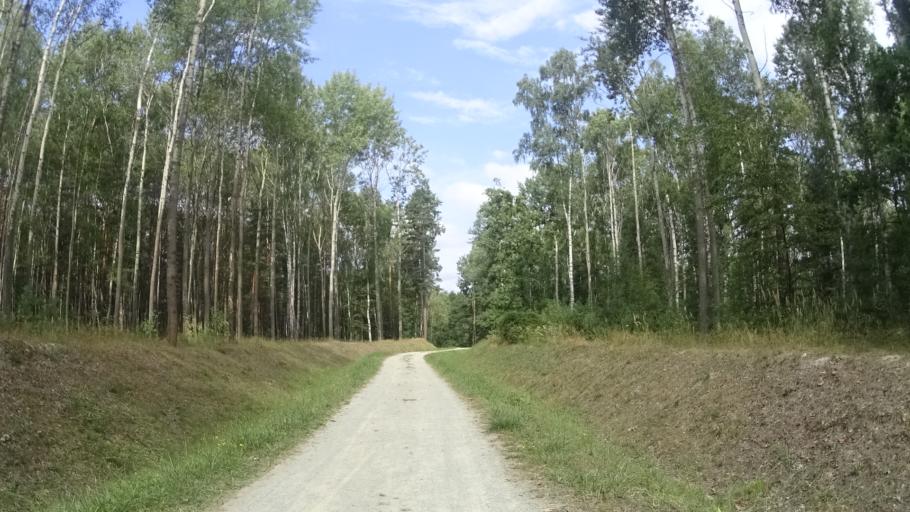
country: PL
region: Lubusz
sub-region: Powiat zarski
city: Leknica
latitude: 51.5341
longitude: 14.7620
